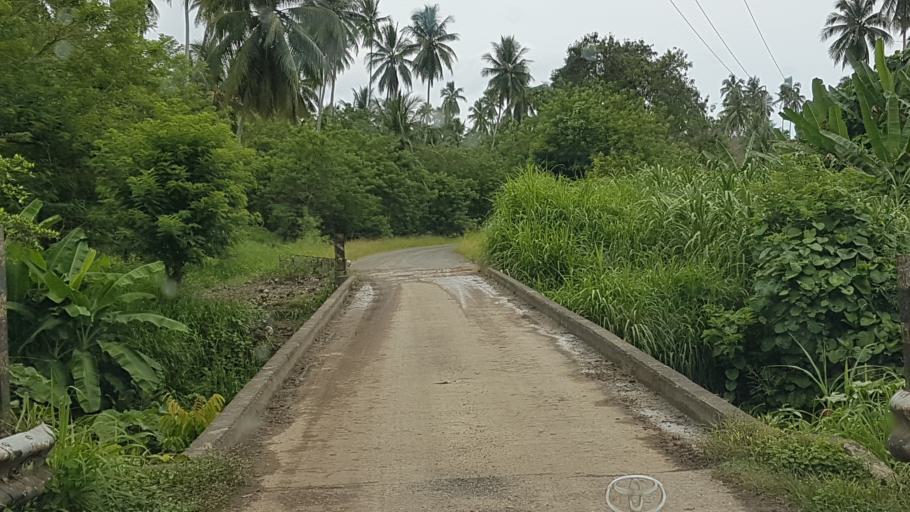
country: PG
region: Madang
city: Madang
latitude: -4.8033
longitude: 145.7328
